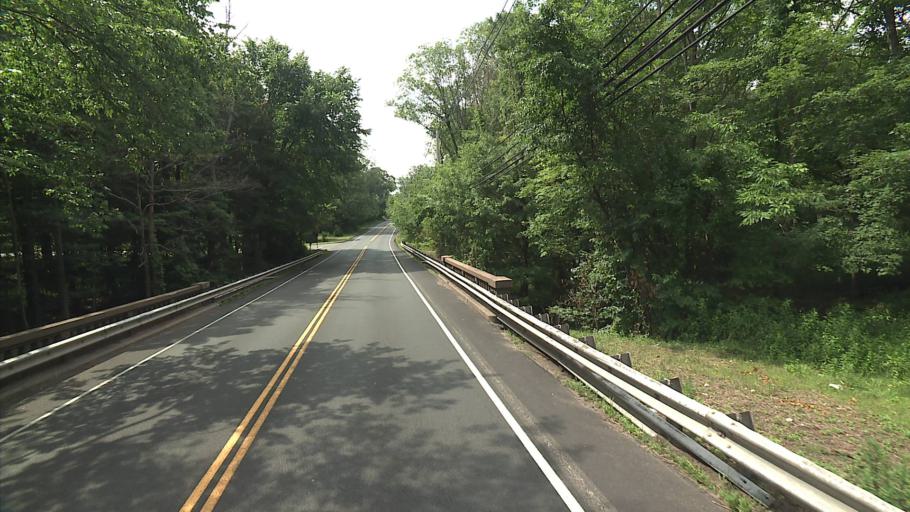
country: US
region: Connecticut
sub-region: New Haven County
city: North Branford
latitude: 41.3824
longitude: -72.7944
